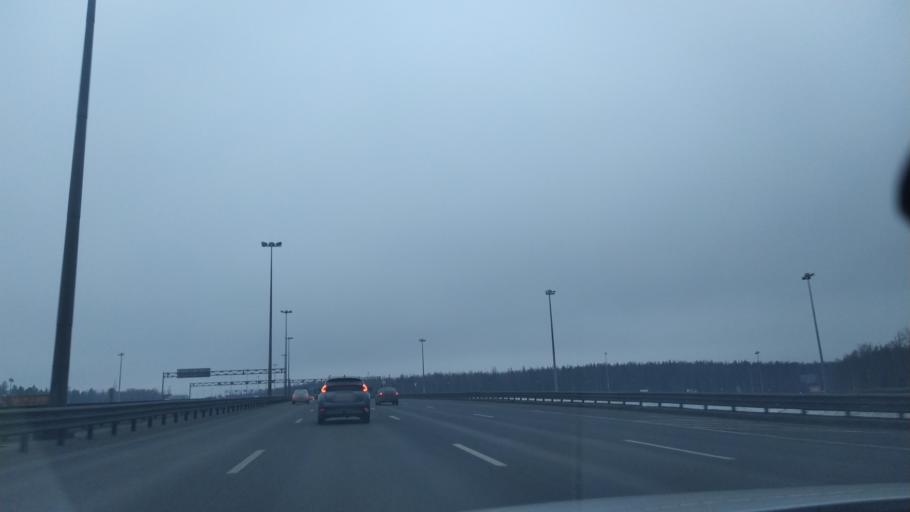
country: RU
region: St.-Petersburg
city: Krasnogvargeisky
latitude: 59.9484
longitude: 30.5425
